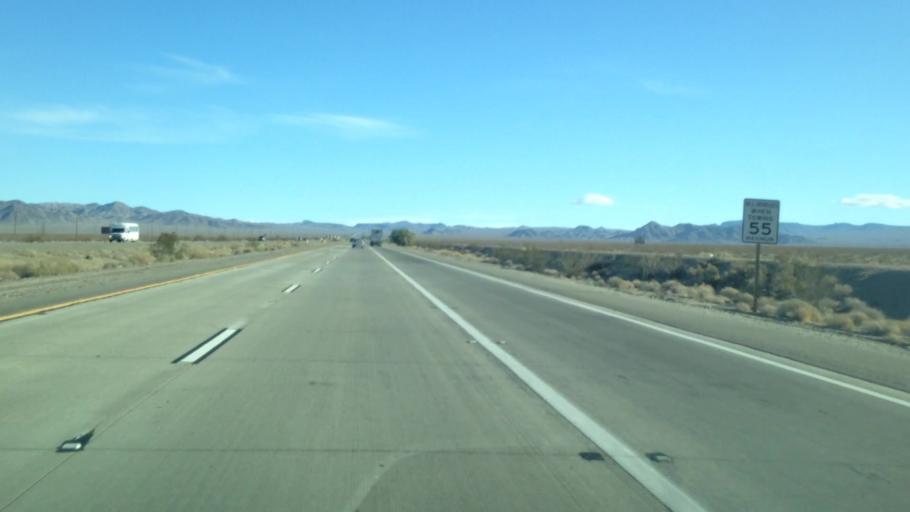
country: US
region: California
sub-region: San Bernardino County
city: Fort Irwin
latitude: 35.2917
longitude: -116.0335
